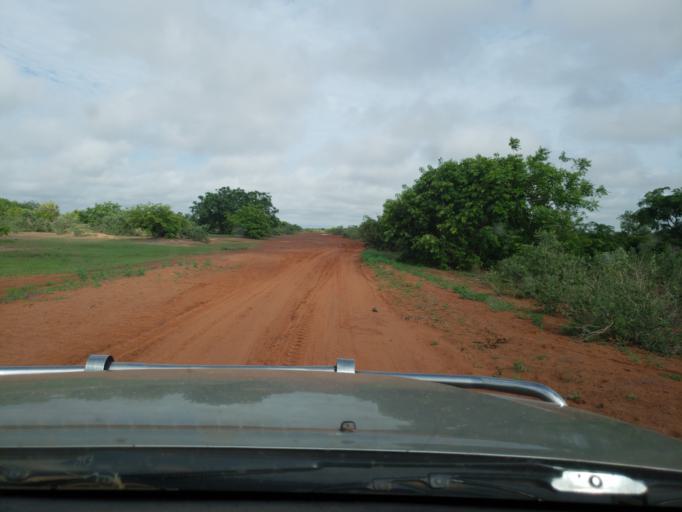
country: ML
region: Sikasso
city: Koutiala
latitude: 12.3925
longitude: -5.9903
